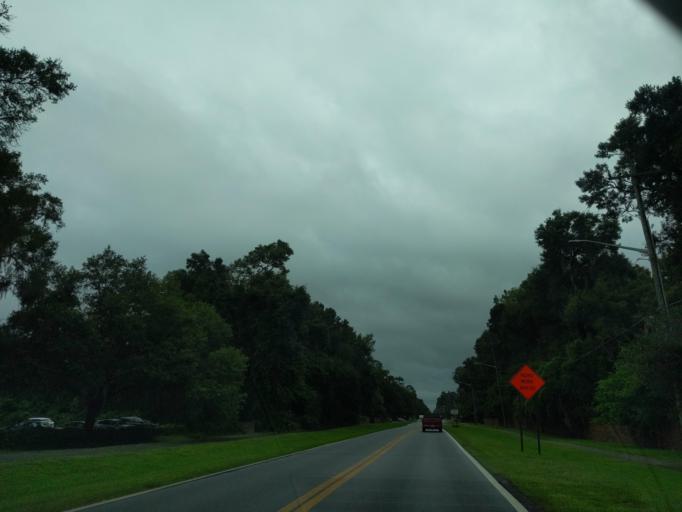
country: US
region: Florida
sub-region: Alachua County
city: Gainesville
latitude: 29.6339
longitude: -82.4225
